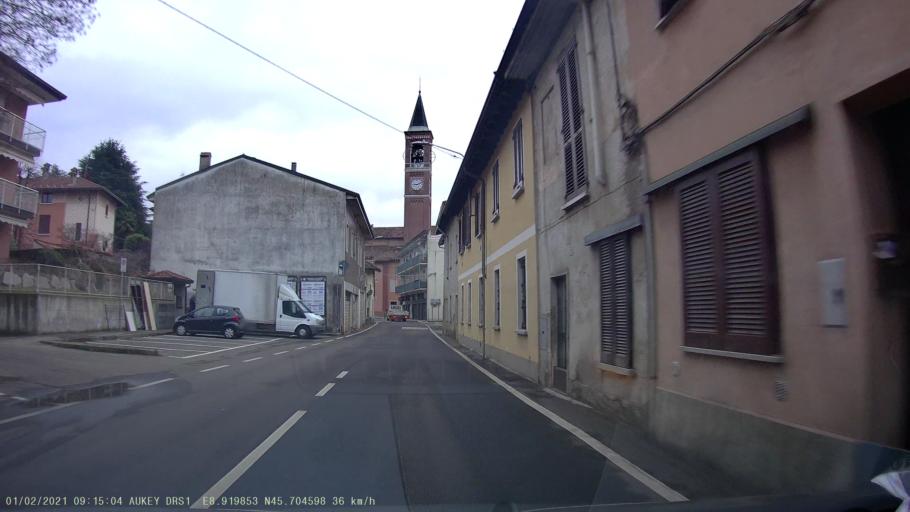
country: IT
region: Lombardy
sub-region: Provincia di Varese
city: Tradate
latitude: 45.7045
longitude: 8.9200
